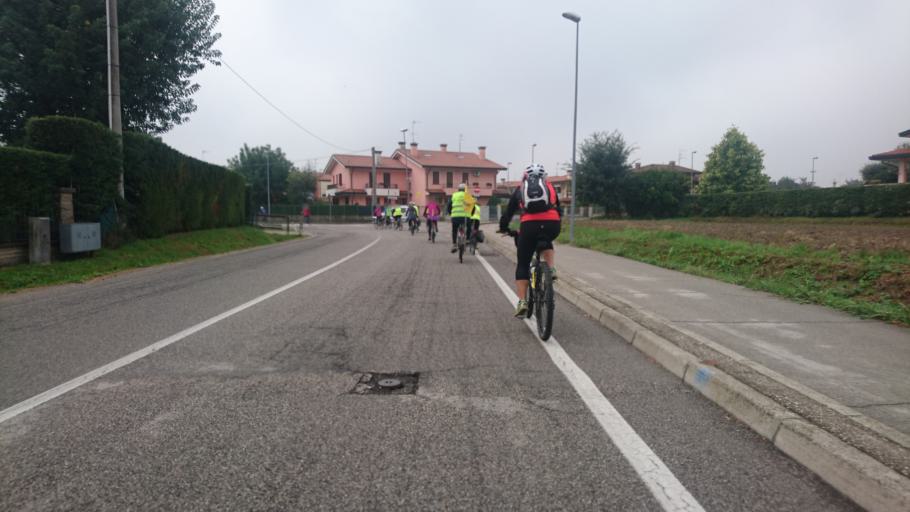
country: IT
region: Veneto
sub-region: Provincia di Padova
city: Monselice
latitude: 45.2347
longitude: 11.7658
